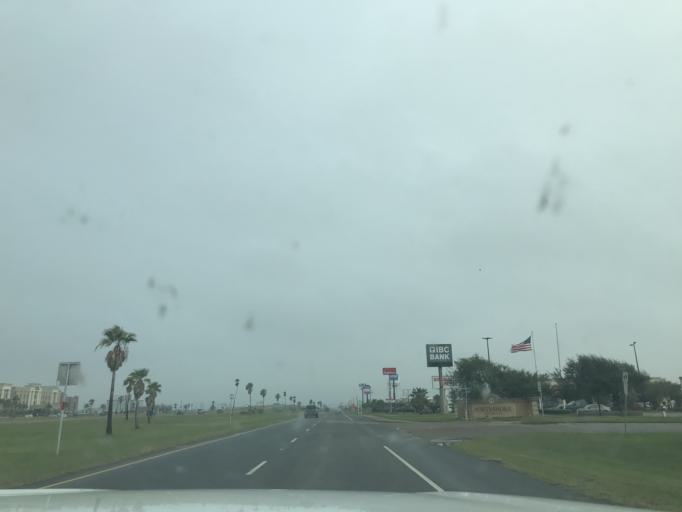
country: US
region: Texas
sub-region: San Patricio County
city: Portland
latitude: 27.8910
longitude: -97.3110
